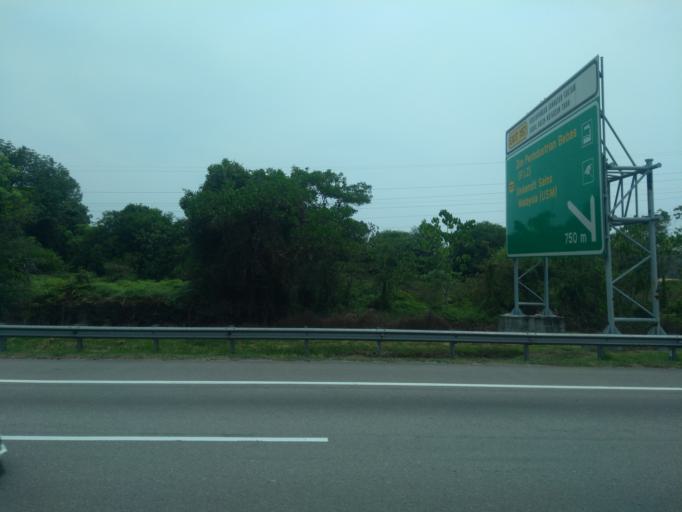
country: MY
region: Penang
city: Nibong Tebal
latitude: 5.2380
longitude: 100.4792
